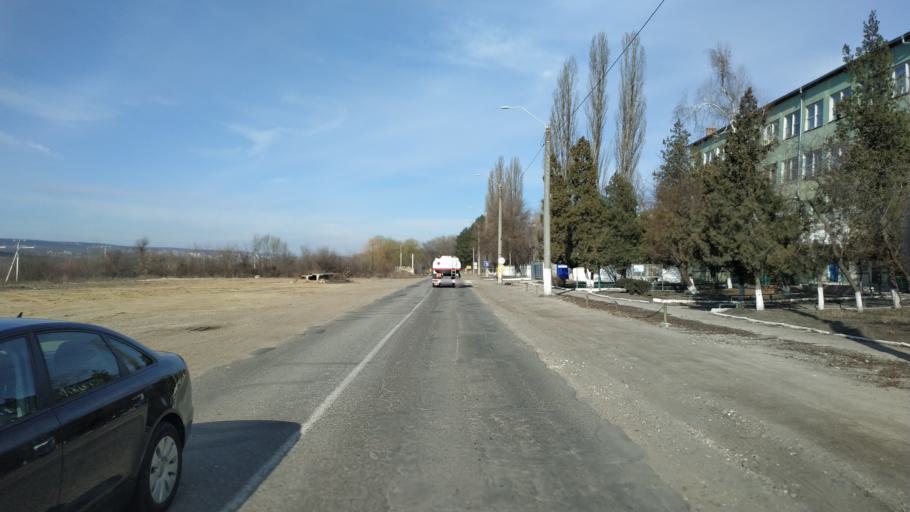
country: MD
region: Laloveni
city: Ialoveni
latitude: 46.9512
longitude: 28.7653
